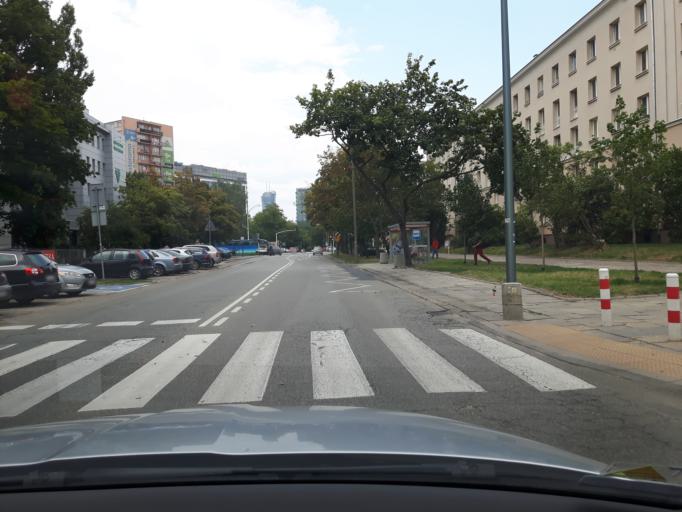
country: PL
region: Masovian Voivodeship
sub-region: Warszawa
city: Ochota
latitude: 52.2179
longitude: 20.9724
